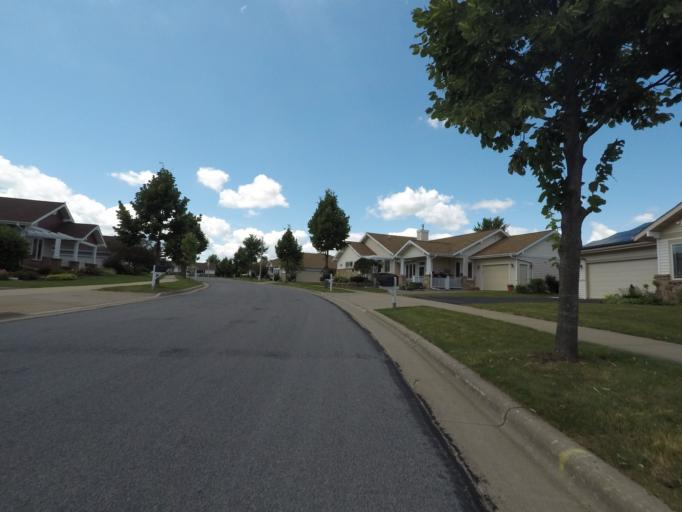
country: US
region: Wisconsin
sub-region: Dane County
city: Middleton
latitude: 43.0712
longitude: -89.5347
